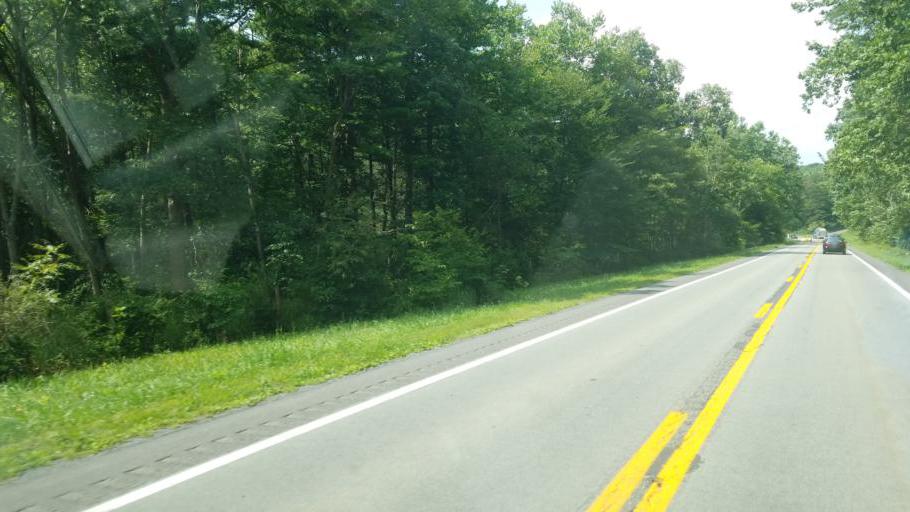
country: US
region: Virginia
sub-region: Frederick County
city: Shawnee Land
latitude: 39.3988
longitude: -78.3800
